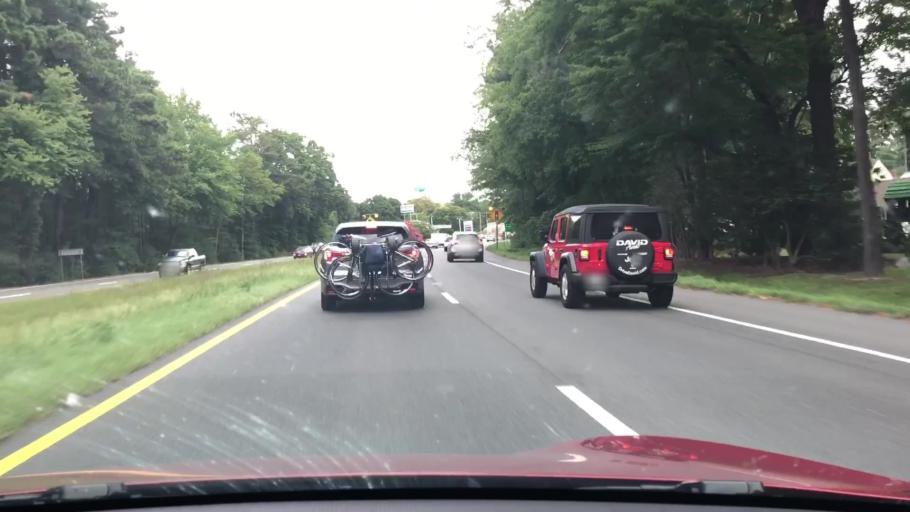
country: US
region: Virginia
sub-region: Northampton County
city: Exmore
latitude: 37.5386
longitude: -75.8263
